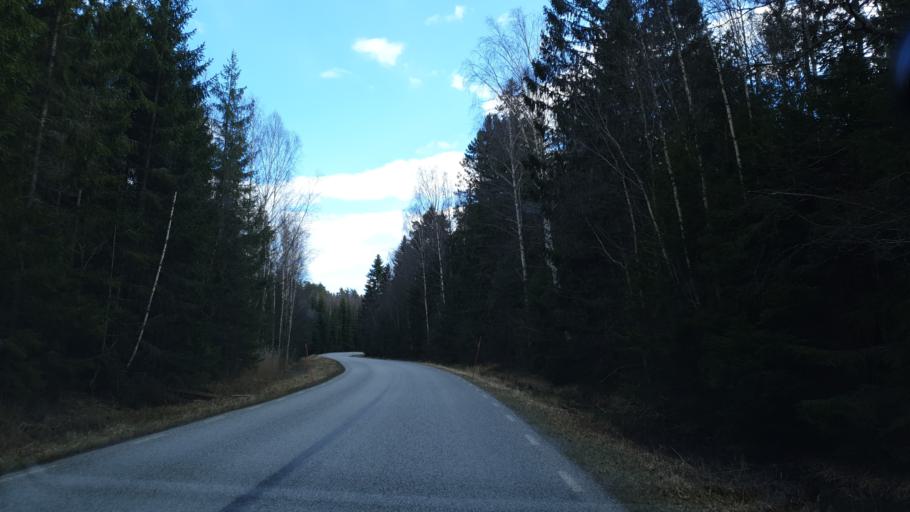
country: SE
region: Stockholm
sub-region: Varmdo Kommun
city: Hemmesta
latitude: 59.2385
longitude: 18.4772
